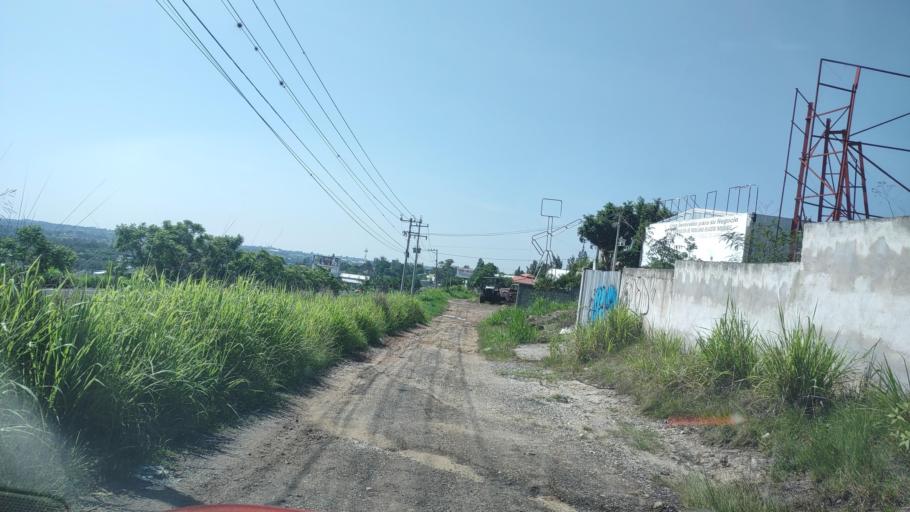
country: MX
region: Veracruz
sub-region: Emiliano Zapata
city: Dos Rios
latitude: 19.4958
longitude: -96.8197
